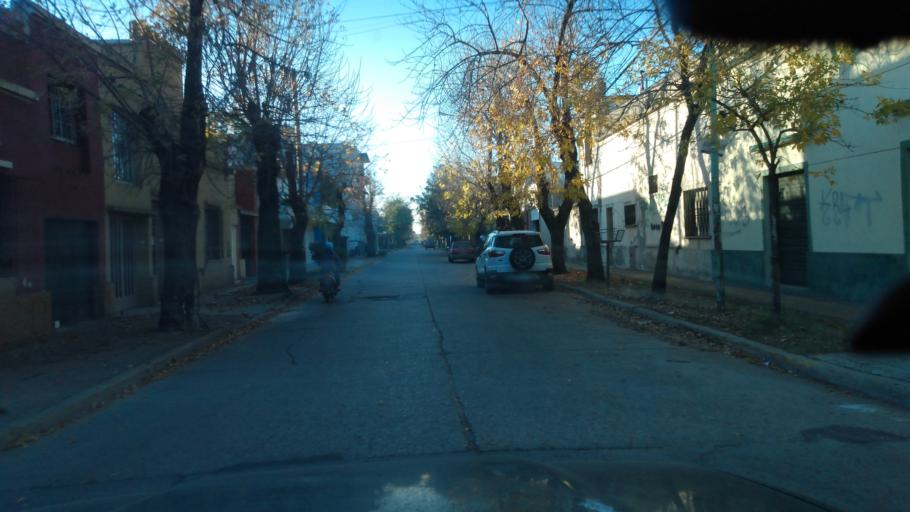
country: AR
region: Buenos Aires
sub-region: Partido de Lujan
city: Lujan
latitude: -34.5612
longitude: -59.1112
